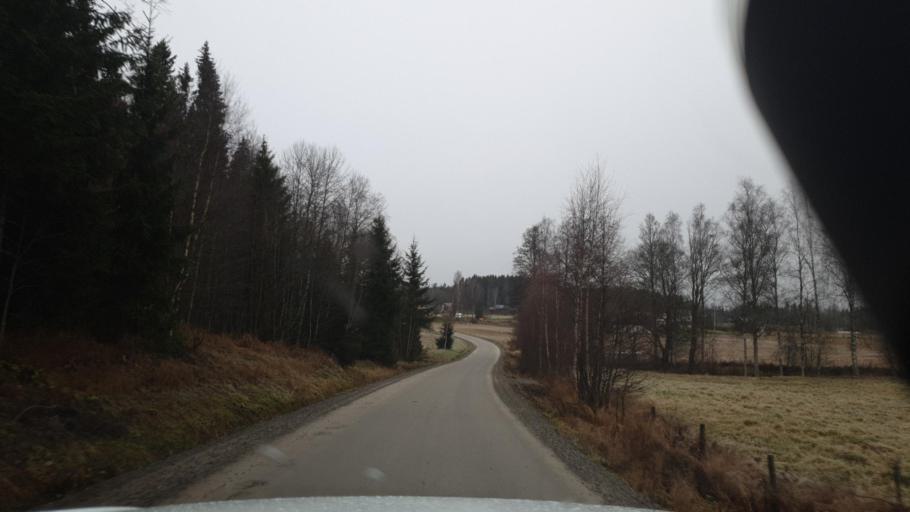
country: SE
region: Vaermland
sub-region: Arvika Kommun
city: Arvika
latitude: 59.6643
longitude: 12.7597
